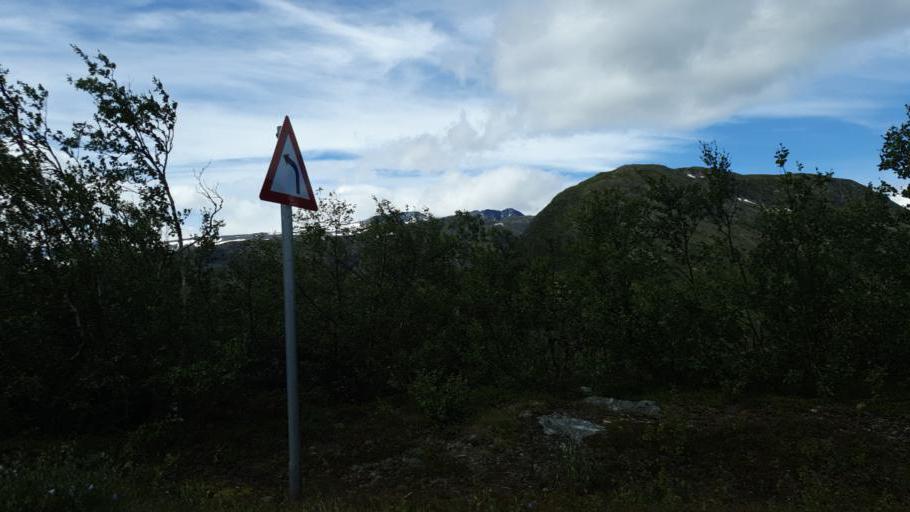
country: NO
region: Oppland
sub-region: Oystre Slidre
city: Heggenes
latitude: 61.4867
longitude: 8.8304
